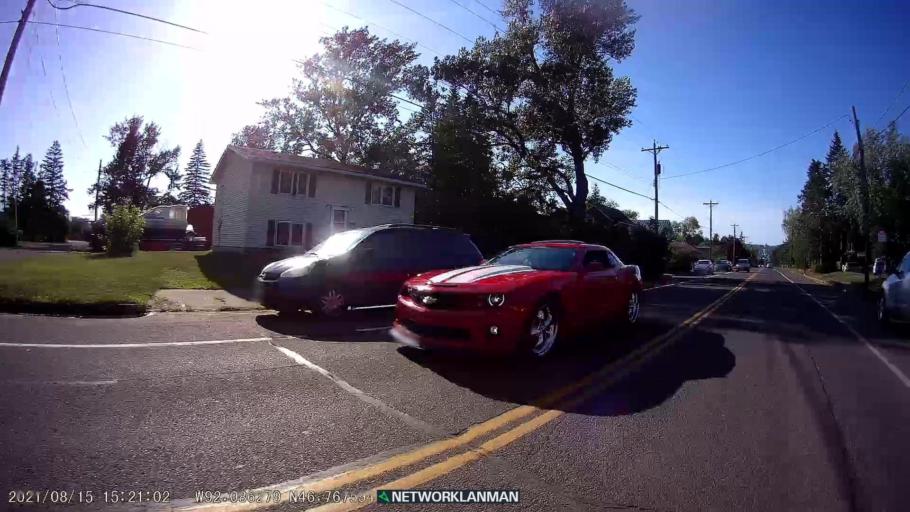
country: US
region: Minnesota
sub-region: Saint Louis County
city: Duluth
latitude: 46.7677
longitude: -92.0864
